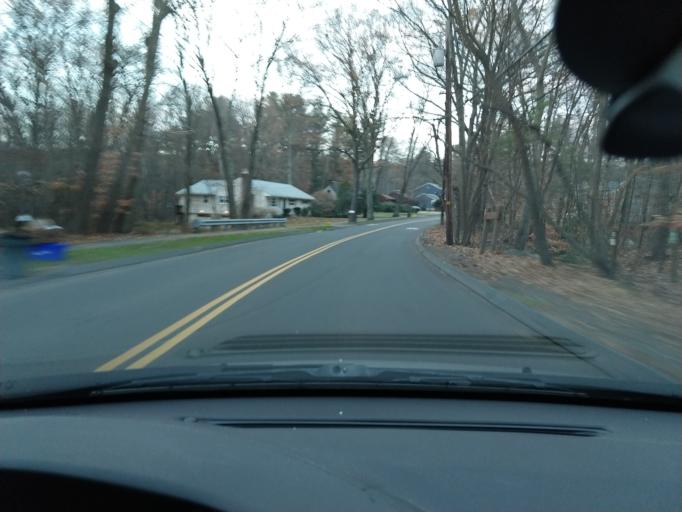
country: US
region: Massachusetts
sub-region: Middlesex County
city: Lexington
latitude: 42.4779
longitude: -71.2408
